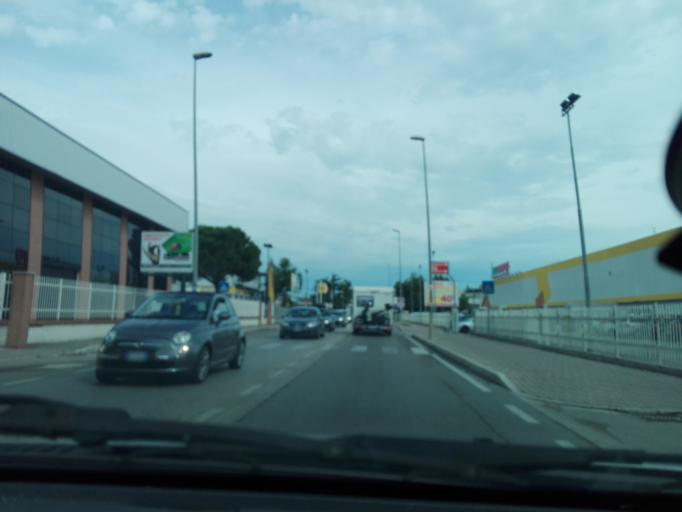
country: IT
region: Abruzzo
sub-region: Provincia di Pescara
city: San Martino Bassa
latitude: 42.5339
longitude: 14.1298
